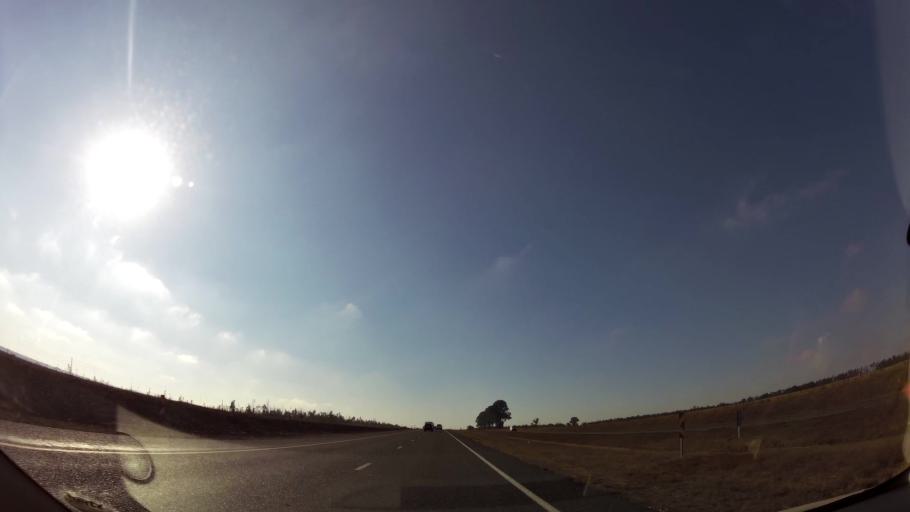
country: ZA
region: Mpumalanga
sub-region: Nkangala District Municipality
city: Delmas
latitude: -26.0185
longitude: 28.9088
